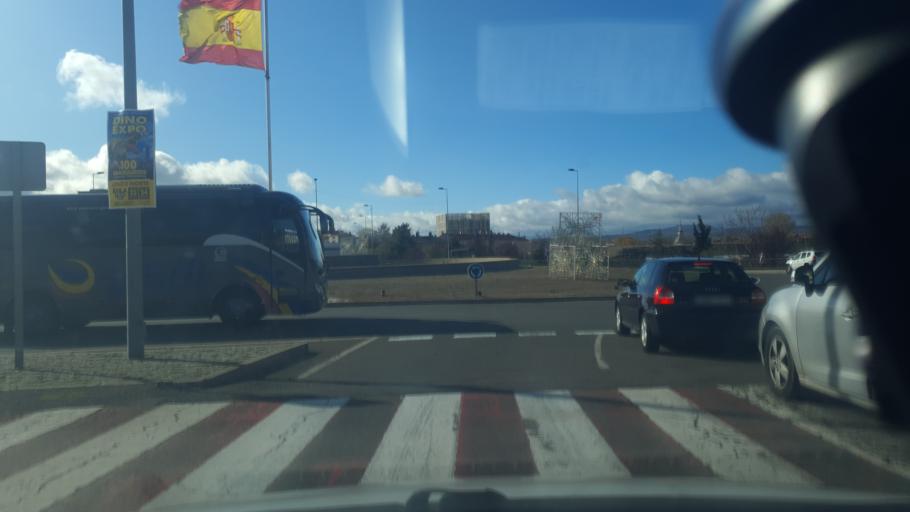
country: ES
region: Castille and Leon
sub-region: Provincia de Avila
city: Avila
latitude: 40.6600
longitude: -4.6788
